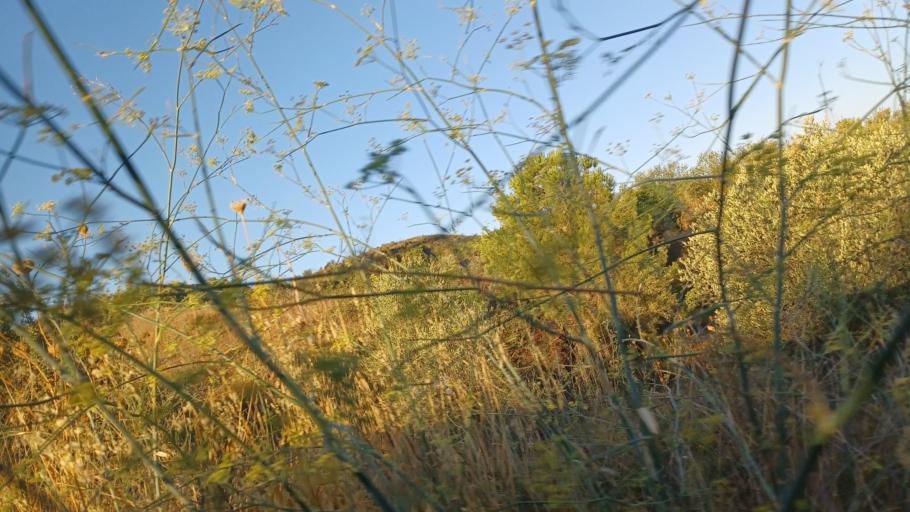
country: CY
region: Pafos
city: Mesogi
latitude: 34.9082
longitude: 32.5244
